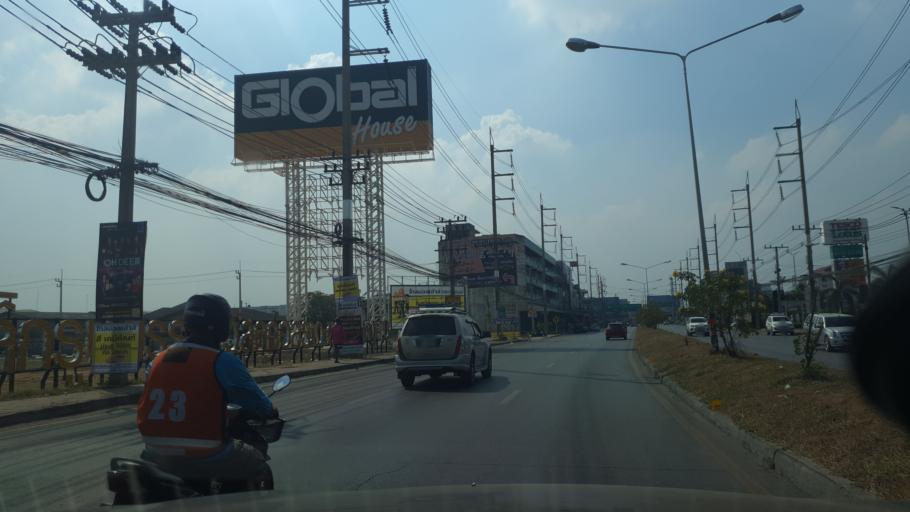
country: TH
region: Samut Sakhon
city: Krathum Baen
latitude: 13.6560
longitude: 100.2744
